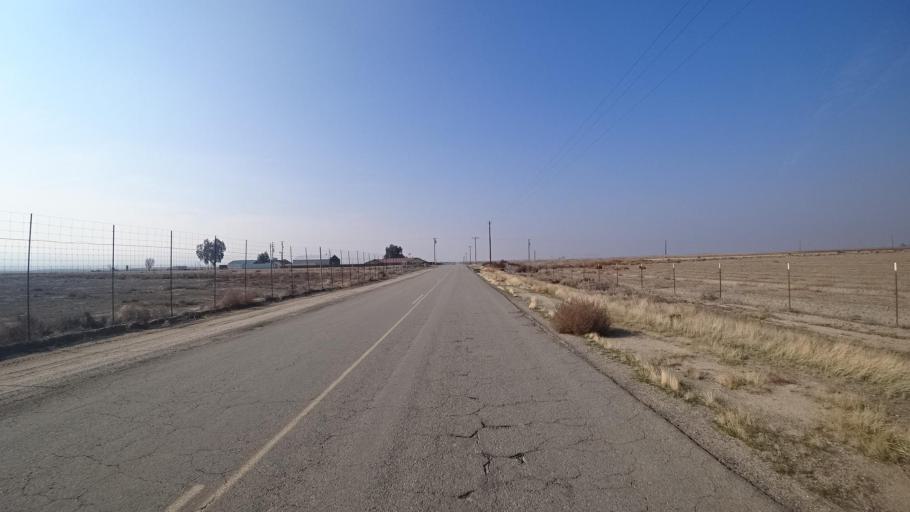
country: US
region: California
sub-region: Kern County
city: Buttonwillow
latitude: 35.3331
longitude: -119.3702
